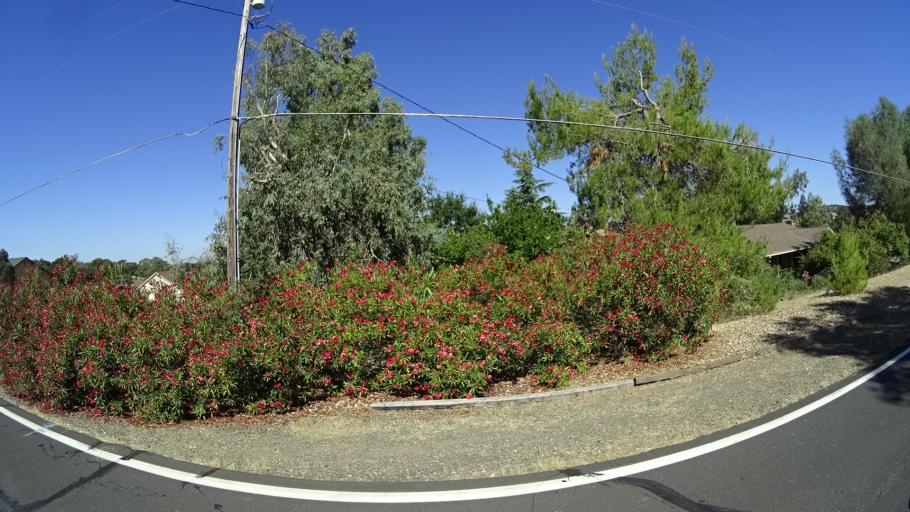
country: US
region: California
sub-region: Calaveras County
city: Rancho Calaveras
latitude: 38.1096
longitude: -120.8777
